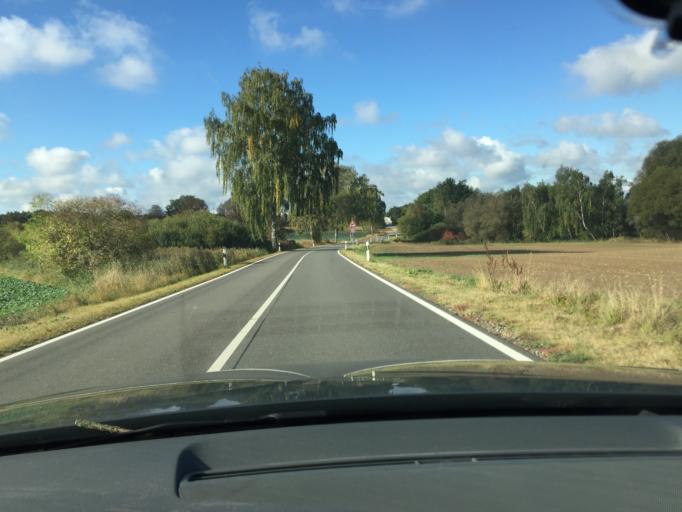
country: DE
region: Mecklenburg-Vorpommern
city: Krakow am See
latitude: 53.6857
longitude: 12.3250
